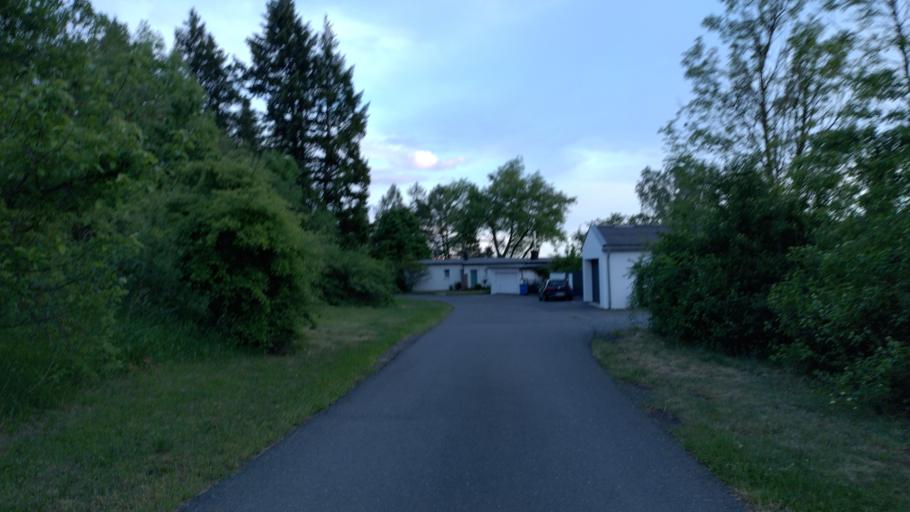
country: DE
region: Bavaria
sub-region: Upper Franconia
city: Bindlach
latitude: 49.9956
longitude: 11.6171
